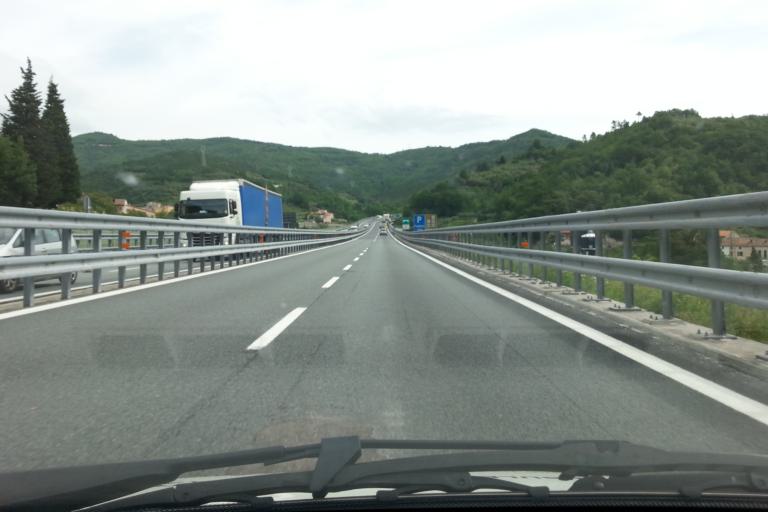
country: IT
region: Liguria
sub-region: Provincia di Savona
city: Feglino
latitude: 44.2153
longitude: 8.3230
